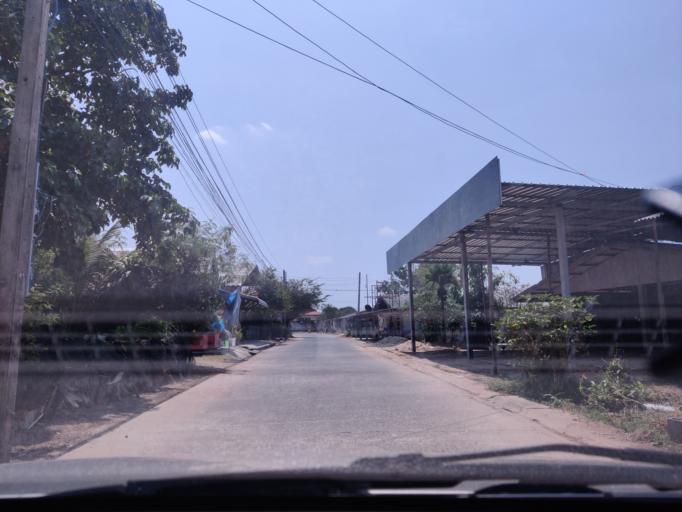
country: TH
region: Sisaket
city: Si Sa Ket
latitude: 15.1034
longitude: 104.3536
